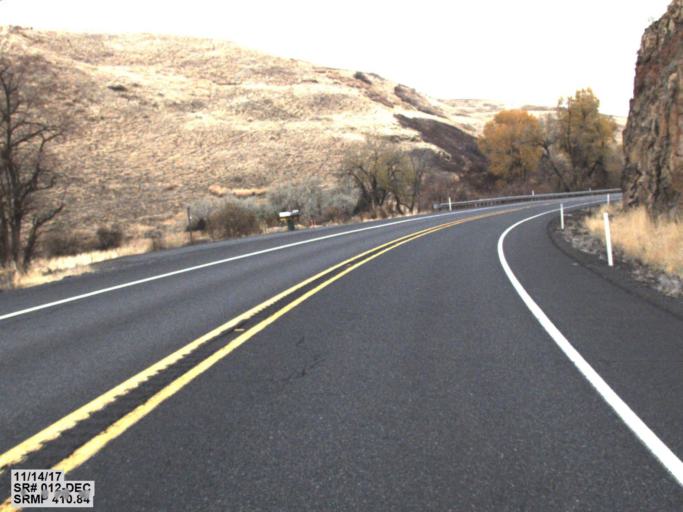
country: US
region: Washington
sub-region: Garfield County
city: Pomeroy
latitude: 46.4474
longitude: -117.4676
